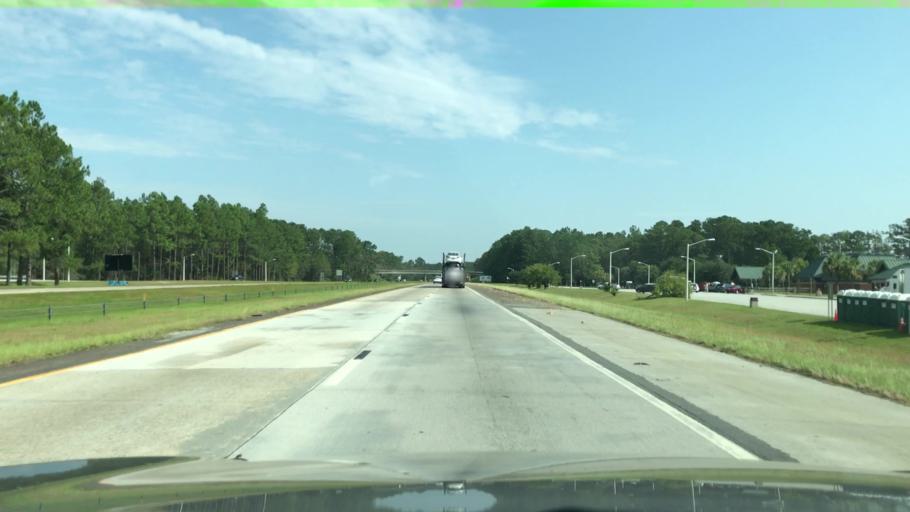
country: US
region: South Carolina
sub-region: Hampton County
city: Yemassee
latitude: 32.8006
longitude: -80.7716
